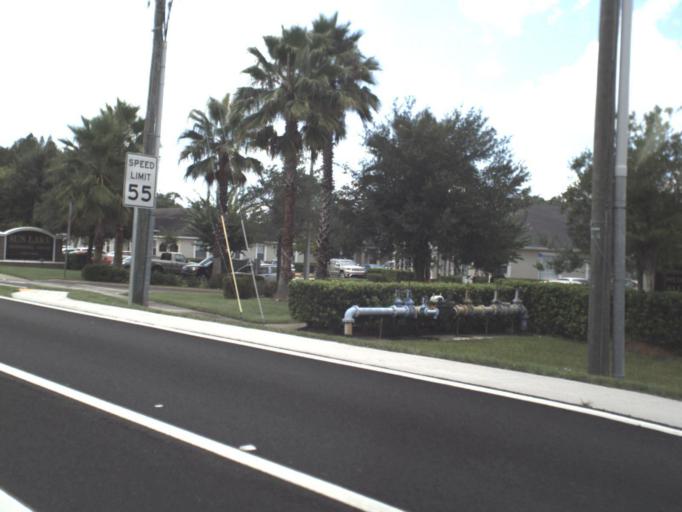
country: US
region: Florida
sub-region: Hillsborough County
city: Cheval
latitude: 28.1519
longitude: -82.4916
